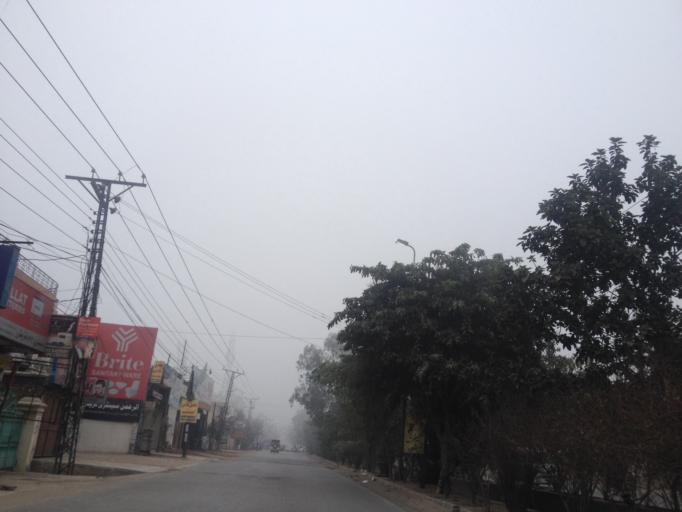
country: PK
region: Punjab
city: Lahore
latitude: 31.4564
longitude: 74.3014
